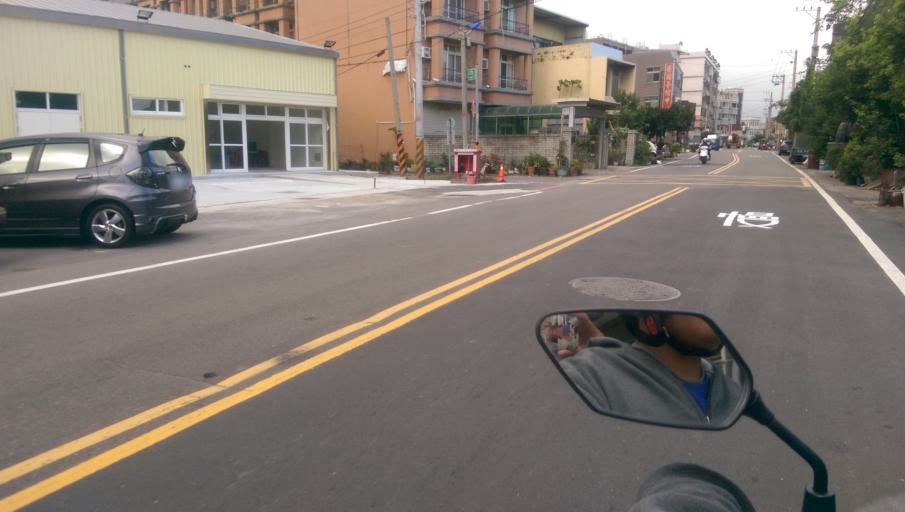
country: TW
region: Taiwan
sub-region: Hsinchu
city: Hsinchu
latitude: 24.8329
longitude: 120.9295
